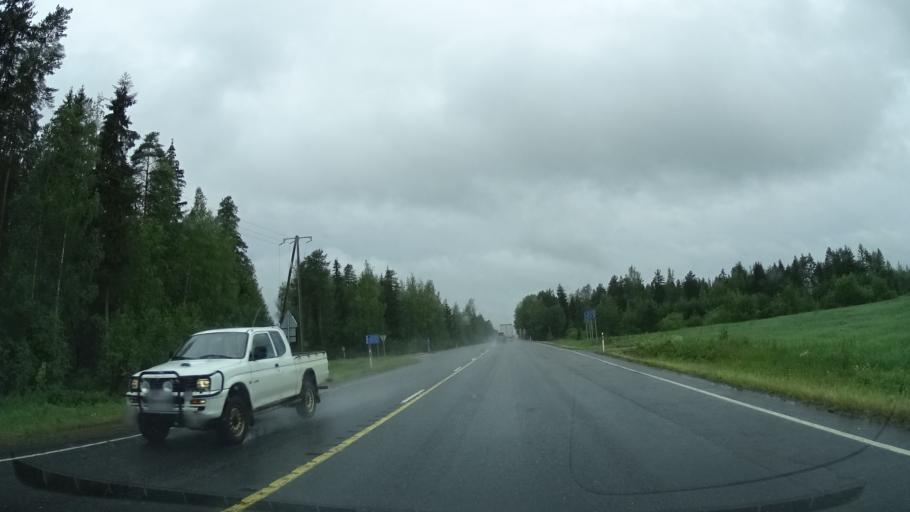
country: FI
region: Haeme
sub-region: Forssa
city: Forssa
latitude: 60.8328
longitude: 23.5574
